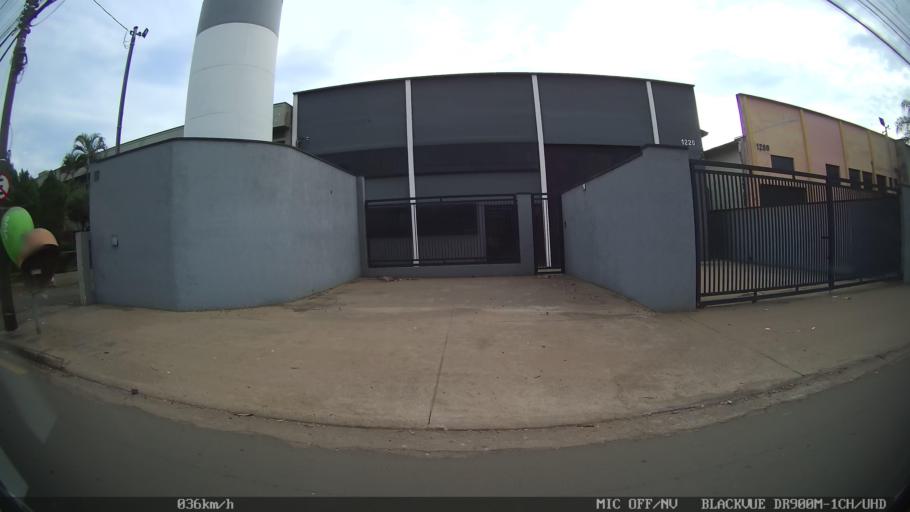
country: BR
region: Sao Paulo
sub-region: Santa Barbara D'Oeste
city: Santa Barbara d'Oeste
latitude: -22.7637
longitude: -47.3851
